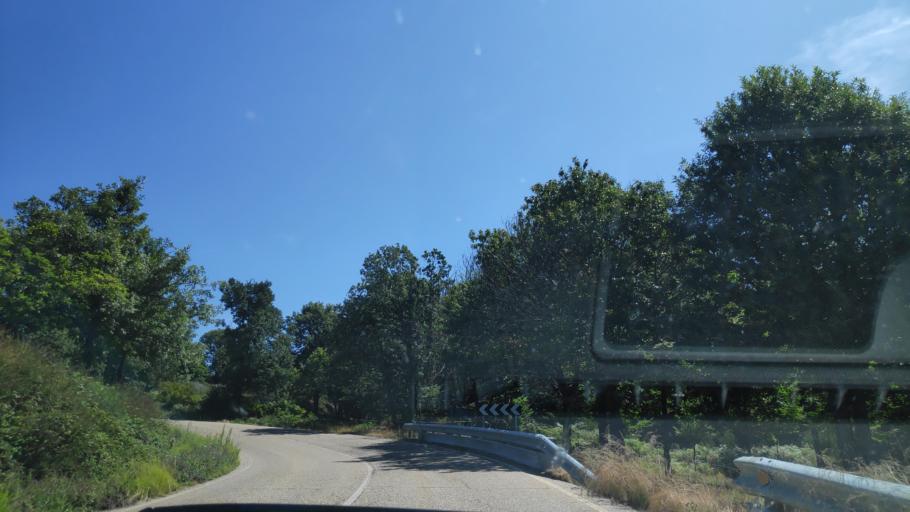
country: ES
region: Castille and Leon
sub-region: Provincia de Zamora
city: Cobreros
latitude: 42.0252
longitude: -6.6842
